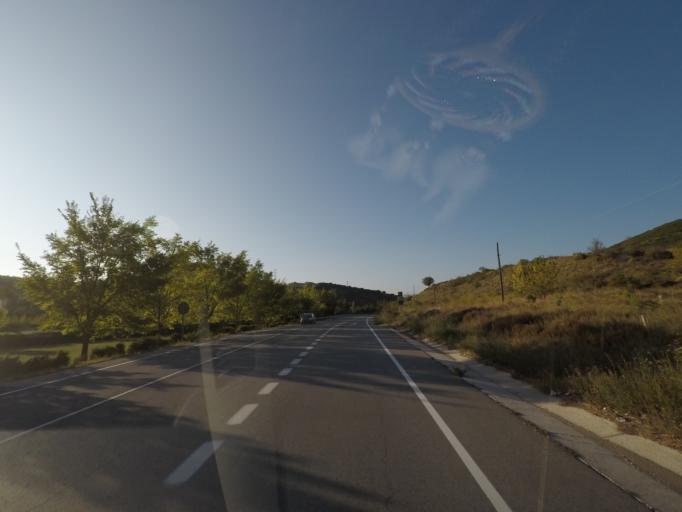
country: ES
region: Navarre
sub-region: Provincia de Navarra
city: Liedena
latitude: 42.6131
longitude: -1.2781
